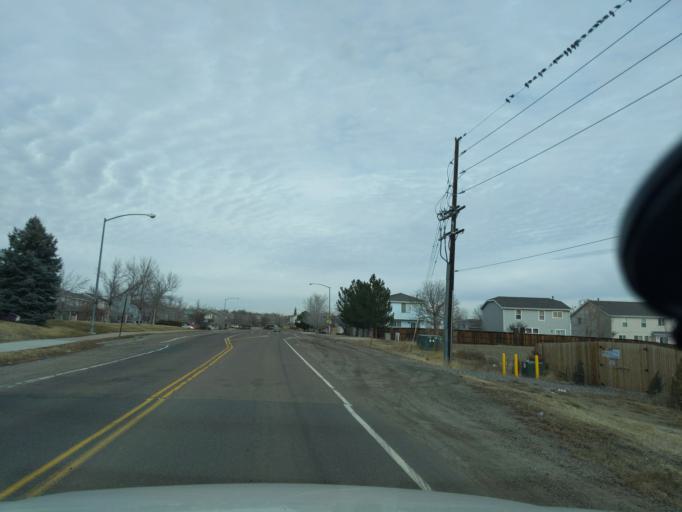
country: US
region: Colorado
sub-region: Adams County
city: Thornton
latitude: 39.8629
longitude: -104.9490
